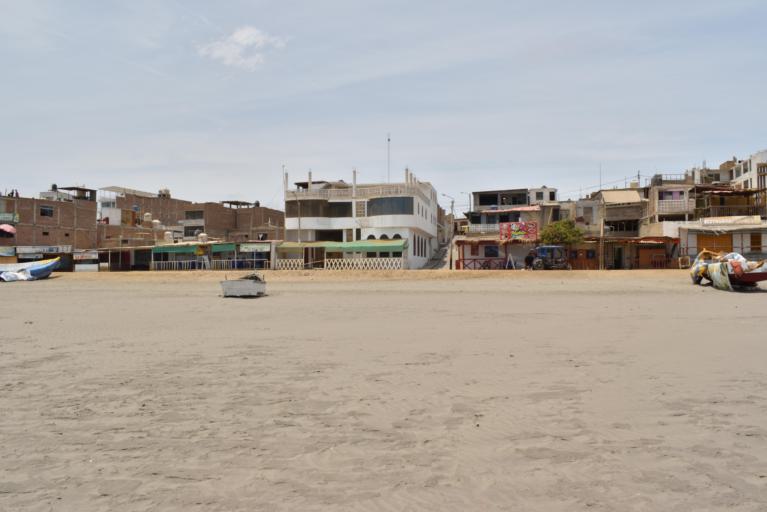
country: PE
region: La Libertad
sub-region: Ascope
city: Paijan
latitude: -7.7017
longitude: -79.4400
